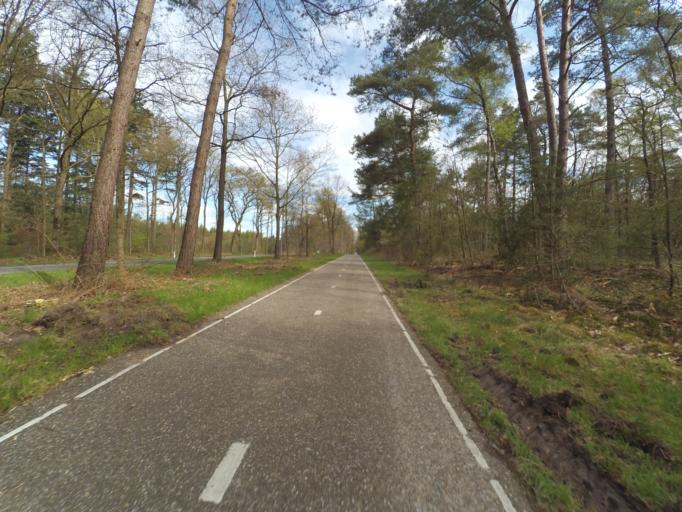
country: NL
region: Gelderland
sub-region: Gemeente Nunspeet
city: Nunspeet
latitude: 52.3221
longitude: 5.7913
